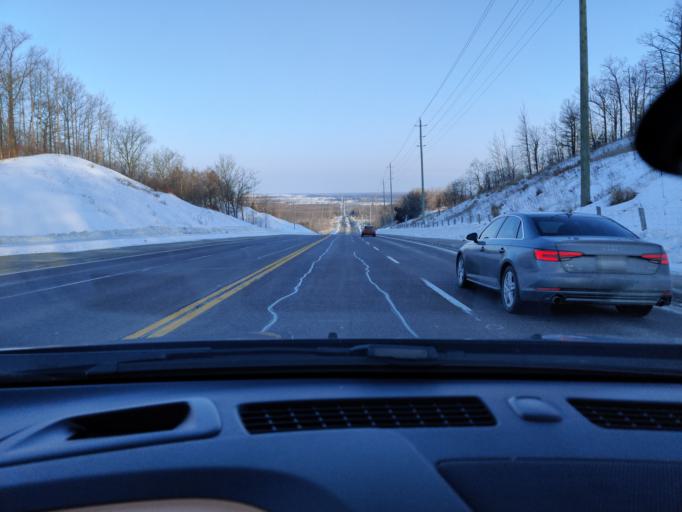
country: CA
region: Ontario
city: Angus
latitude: 44.3990
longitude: -79.8029
